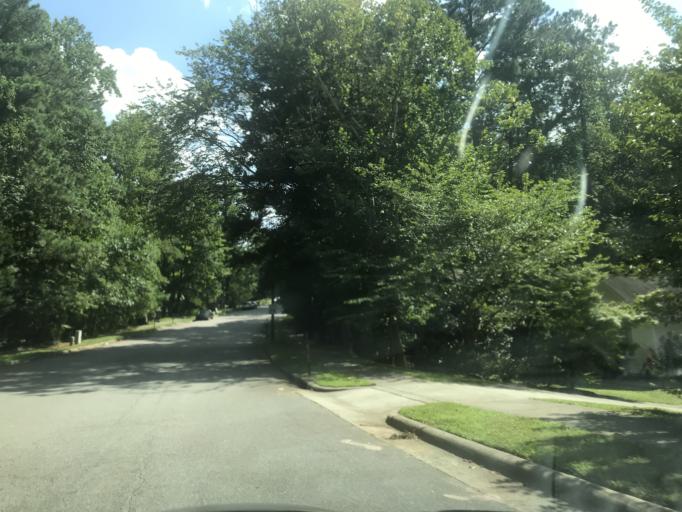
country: US
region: North Carolina
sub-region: Wake County
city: West Raleigh
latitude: 35.8720
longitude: -78.7067
